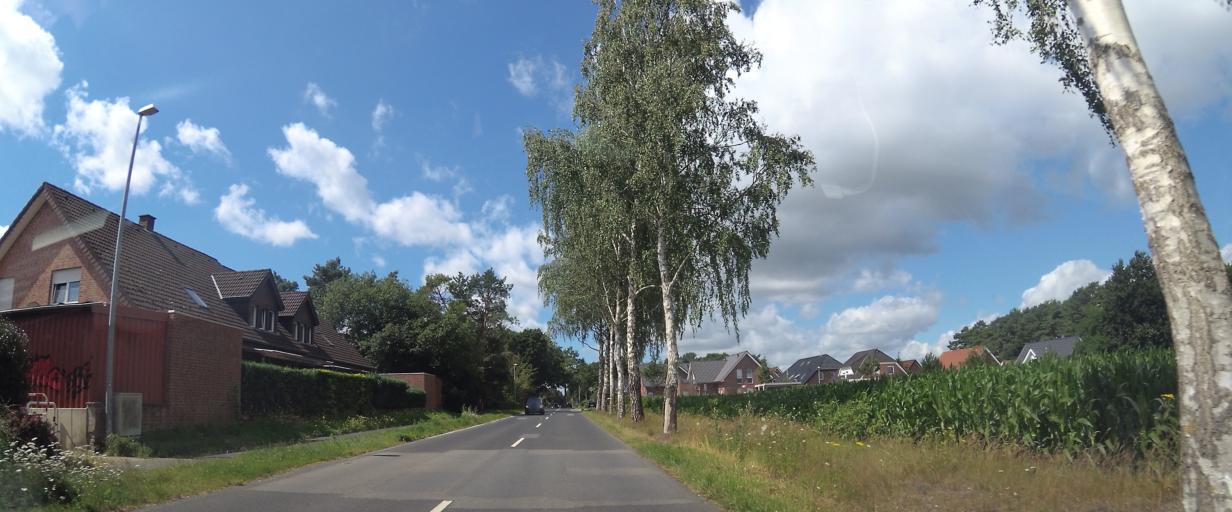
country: DE
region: Lower Saxony
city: Haren
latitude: 52.7909
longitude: 7.2933
